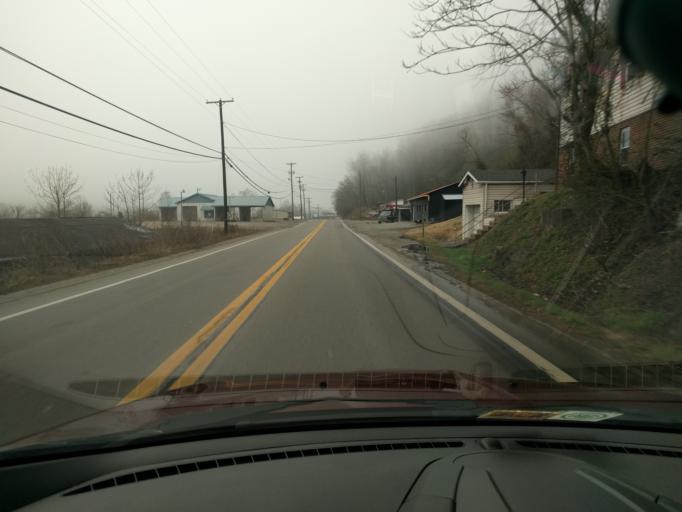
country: US
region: West Virginia
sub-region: Kanawha County
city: Chesapeake
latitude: 38.2099
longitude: -81.4665
